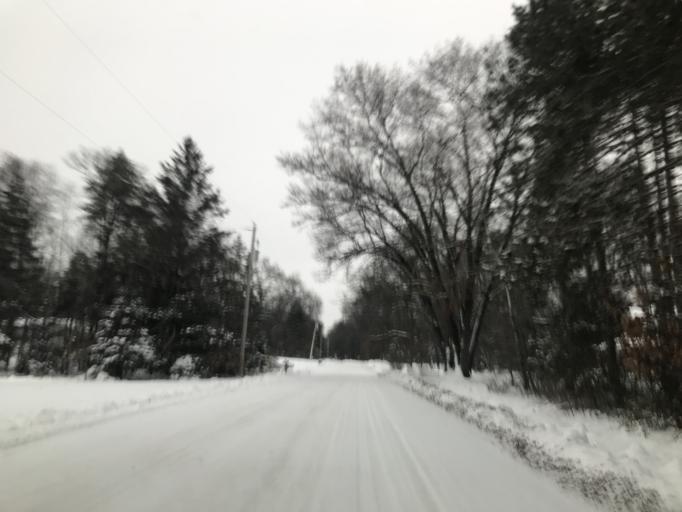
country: US
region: Wisconsin
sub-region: Marinette County
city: Peshtigo
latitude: 45.0354
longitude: -87.7191
